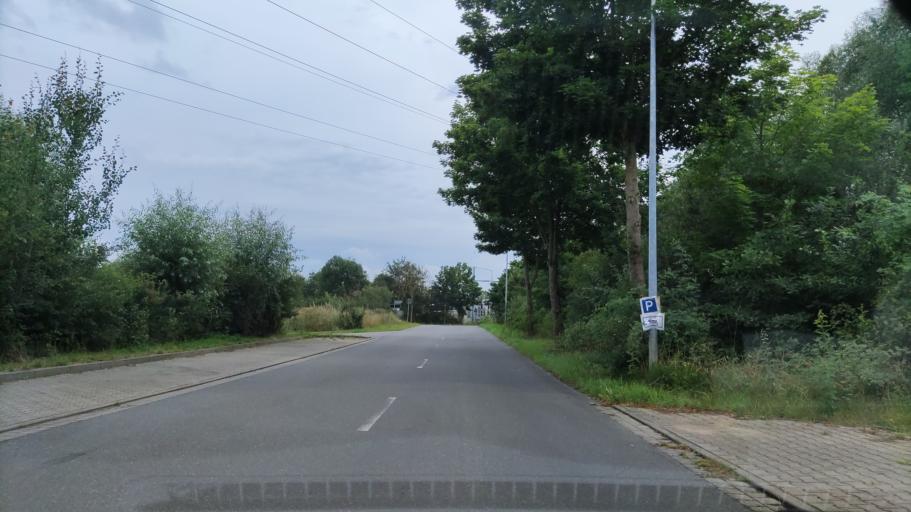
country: DE
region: Lower Saxony
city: Luechow
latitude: 52.9850
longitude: 11.1637
